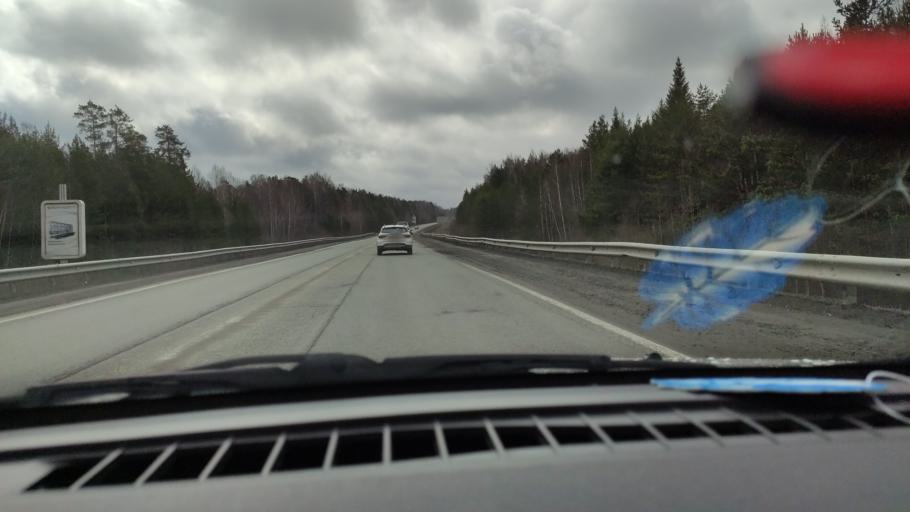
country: RU
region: Sverdlovsk
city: Talitsa
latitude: 56.8624
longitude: 60.0507
